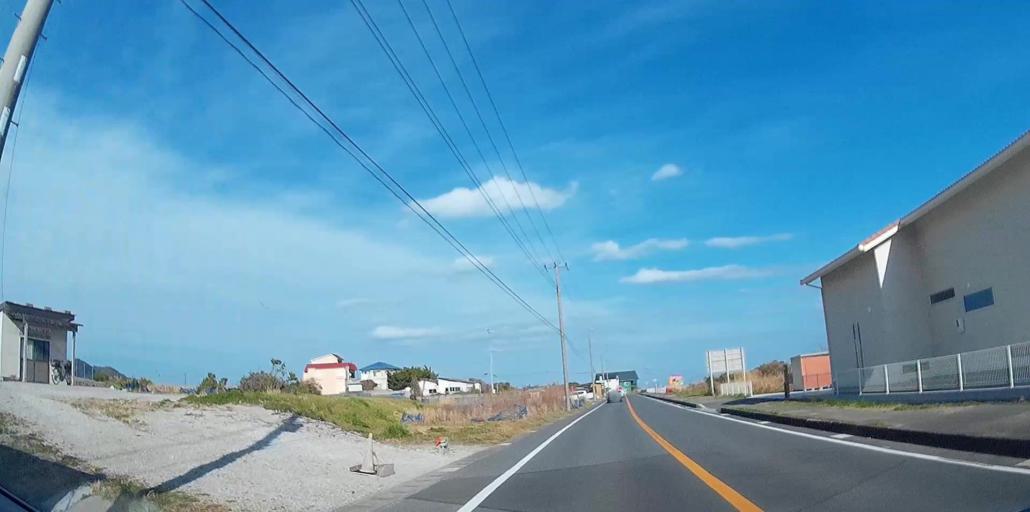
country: JP
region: Chiba
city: Tateyama
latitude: 34.9175
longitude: 139.9365
